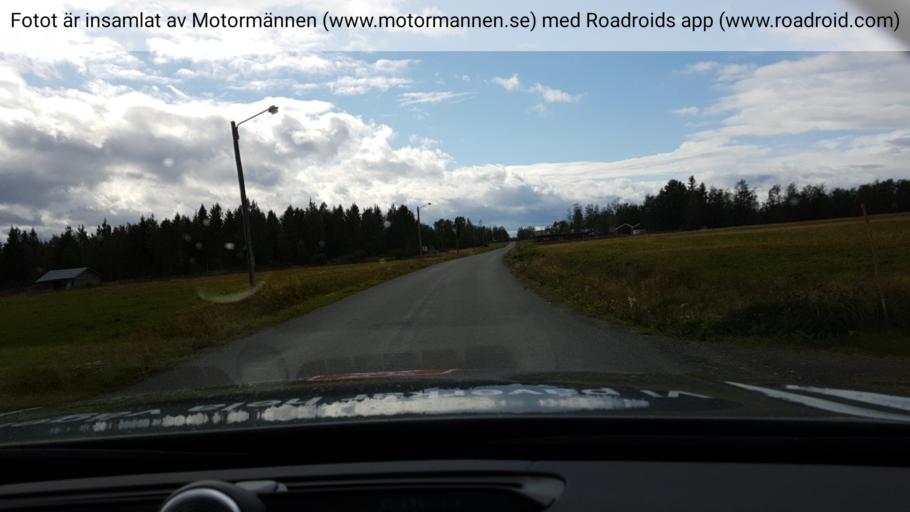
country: SE
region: Jaemtland
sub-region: OEstersunds Kommun
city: Lit
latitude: 63.6821
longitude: 14.8439
